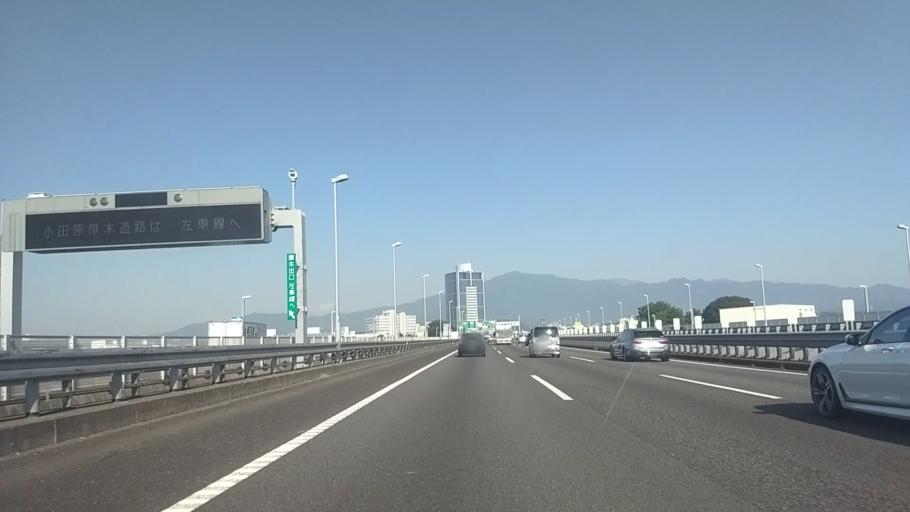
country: JP
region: Kanagawa
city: Atsugi
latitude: 35.4218
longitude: 139.3717
